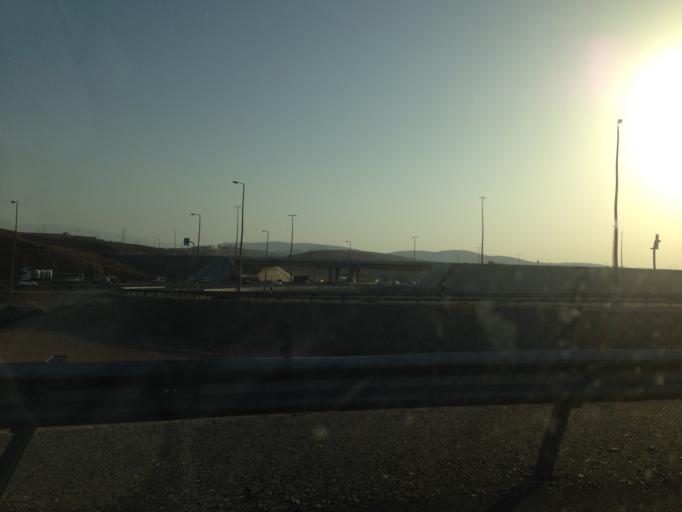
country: OM
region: Muhafazat Masqat
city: Bawshar
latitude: 23.5626
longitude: 58.3410
